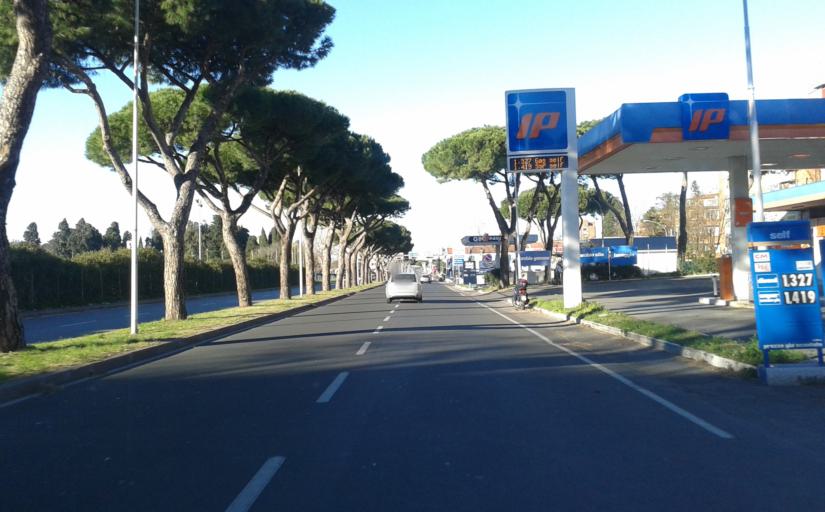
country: IT
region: Tuscany
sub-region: Provincia di Livorno
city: Livorno
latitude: 43.5605
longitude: 10.3264
